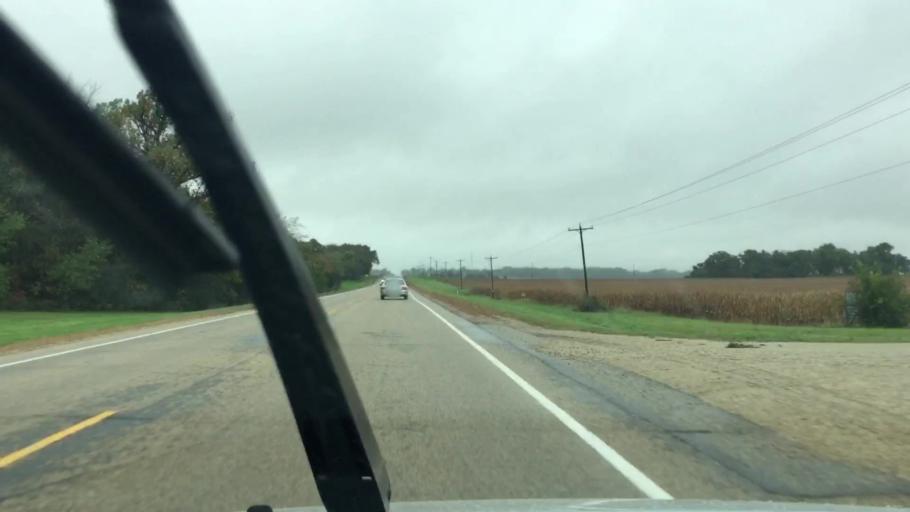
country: US
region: Wisconsin
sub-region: Walworth County
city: Whitewater
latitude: 42.8572
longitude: -88.6712
